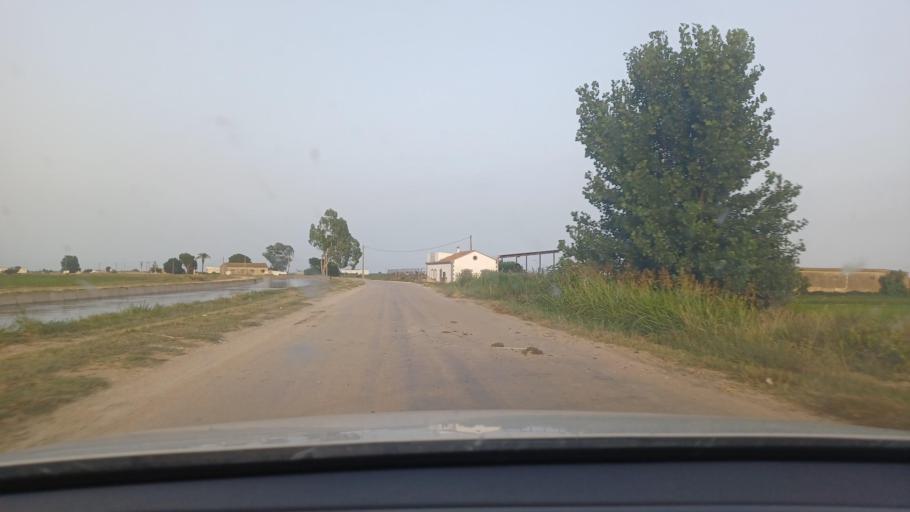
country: ES
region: Catalonia
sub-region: Provincia de Tarragona
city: Amposta
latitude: 40.6991
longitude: 0.6126
